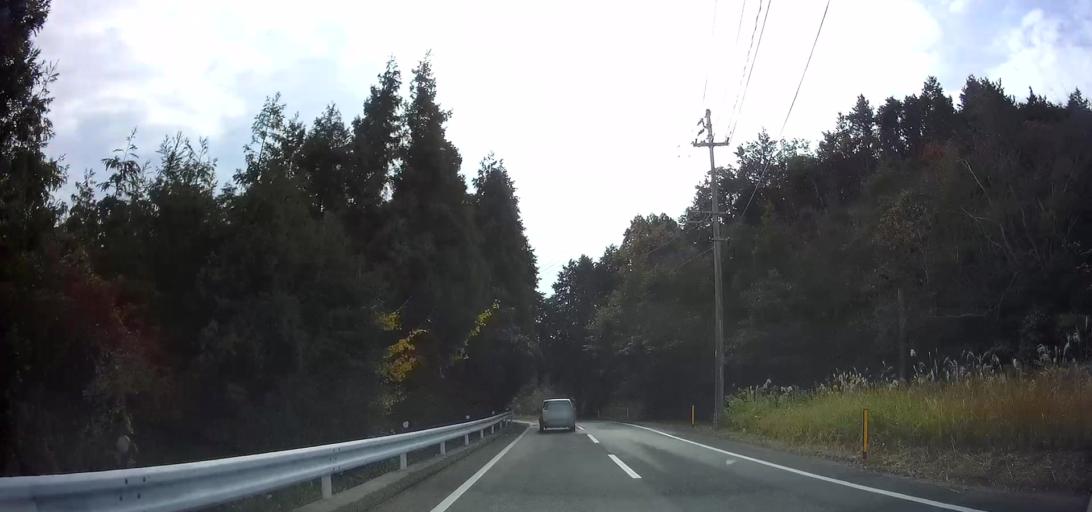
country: JP
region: Nagasaki
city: Shimabara
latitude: 32.6939
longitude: 130.2552
